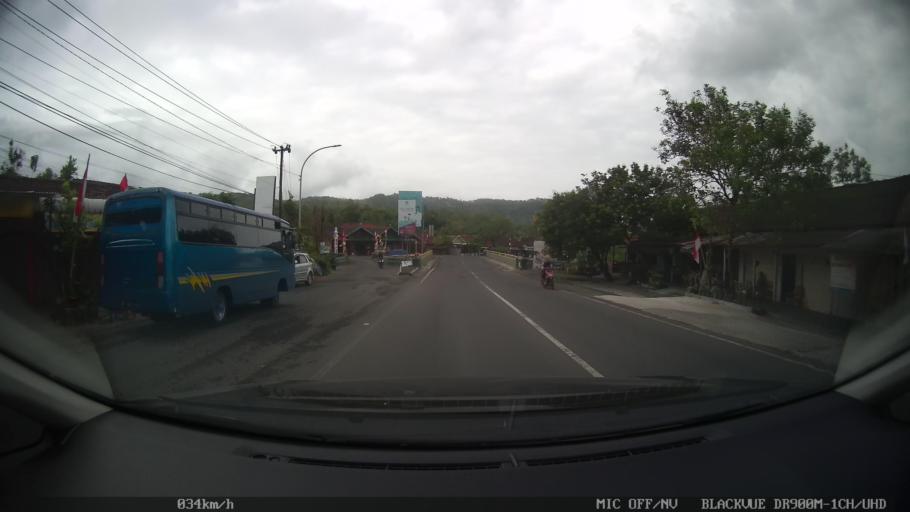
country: ID
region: Daerah Istimewa Yogyakarta
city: Depok
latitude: -7.8461
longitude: 110.4400
